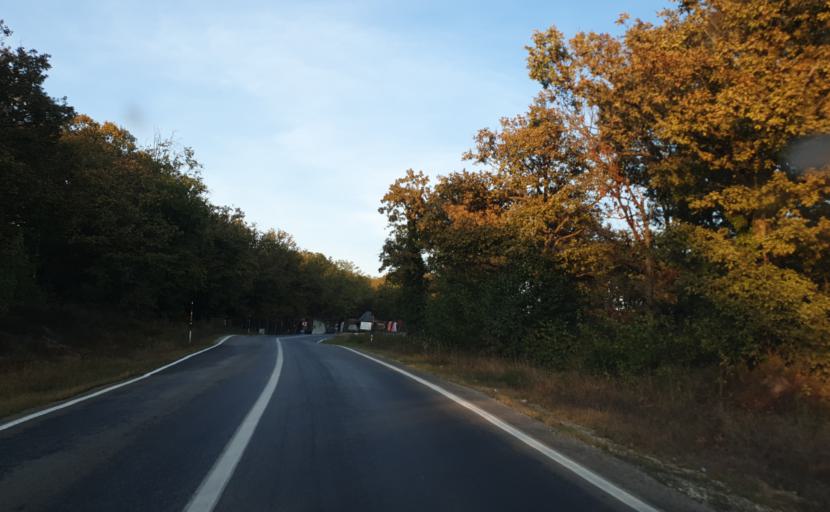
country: TR
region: Kirklareli
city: Sergen
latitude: 41.8397
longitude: 27.7991
